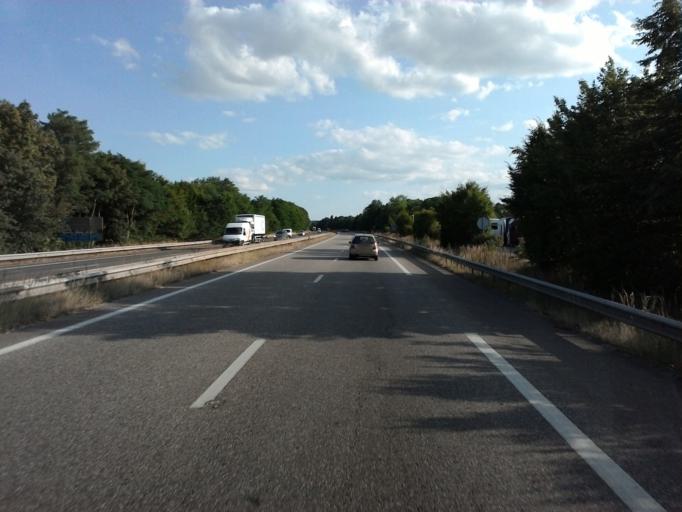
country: FR
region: Lorraine
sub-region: Departement de Meurthe-et-Moselle
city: Richardmenil
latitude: 48.6070
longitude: 6.1743
